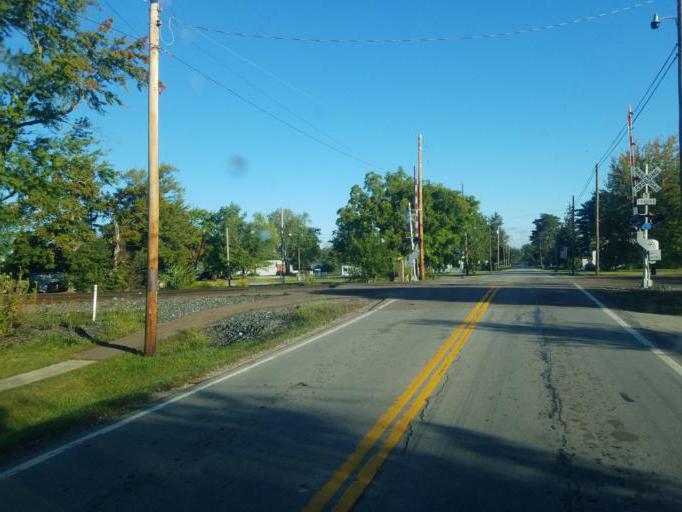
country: US
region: Ohio
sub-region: Lorain County
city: Wellington
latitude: 41.1255
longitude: -82.3045
